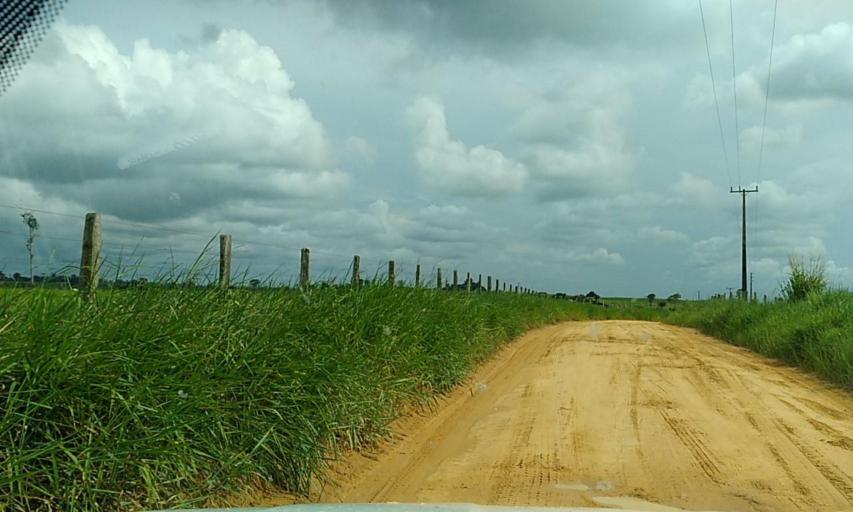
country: BR
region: Para
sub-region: Altamira
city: Altamira
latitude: -3.2426
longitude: -52.6947
